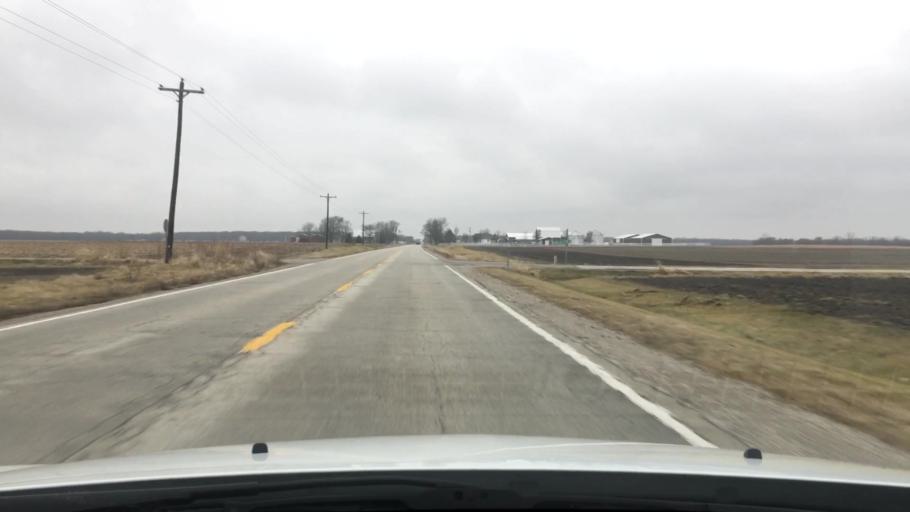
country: US
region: Illinois
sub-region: Iroquois County
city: Watseka
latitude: 40.8879
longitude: -87.8066
